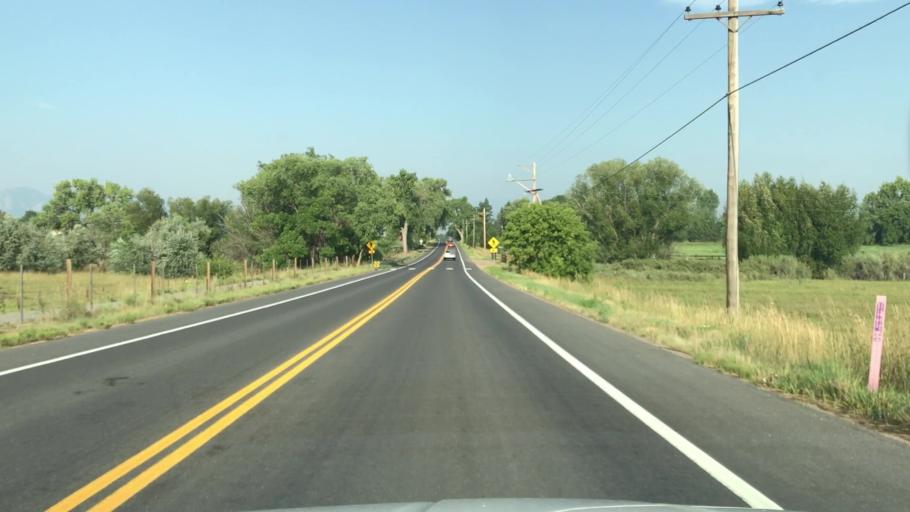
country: US
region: Colorado
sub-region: Boulder County
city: Gunbarrel
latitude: 40.0401
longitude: -105.1448
